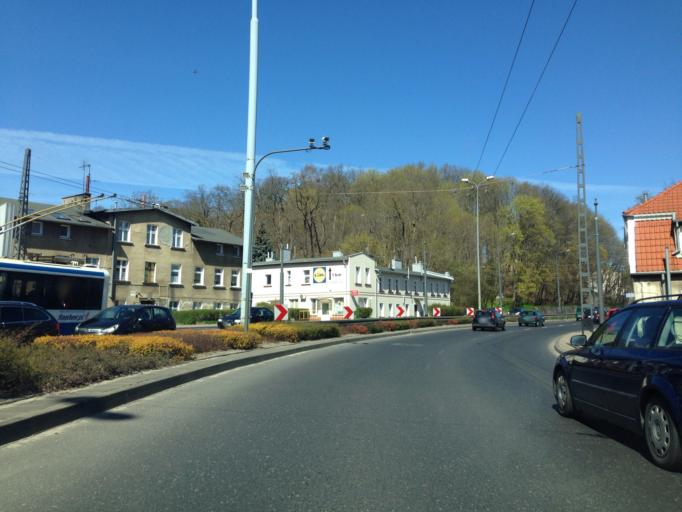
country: PL
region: Pomeranian Voivodeship
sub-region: Sopot
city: Sopot
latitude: 54.4501
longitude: 18.5550
